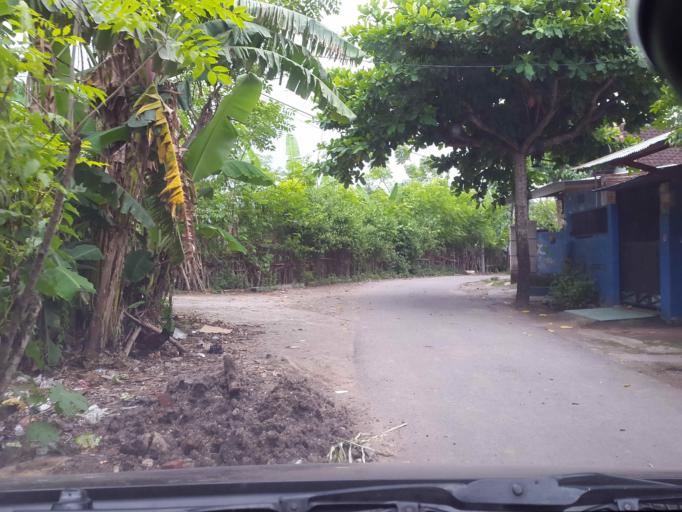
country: ID
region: West Nusa Tenggara
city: Mambalan
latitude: -8.5495
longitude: 116.0830
